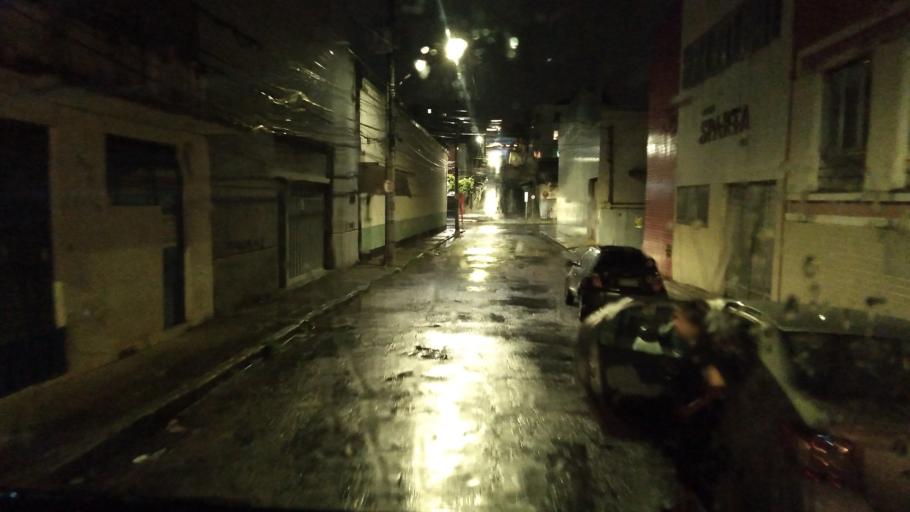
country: BR
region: Minas Gerais
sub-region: Belo Horizonte
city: Belo Horizonte
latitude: -19.9119
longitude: -43.9754
